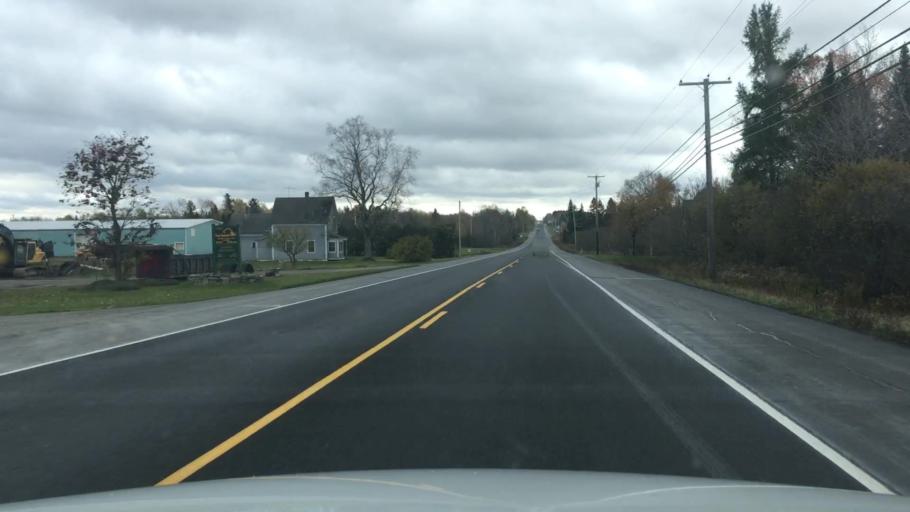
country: US
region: Maine
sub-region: Aroostook County
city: Houlton
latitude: 46.2474
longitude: -67.8408
